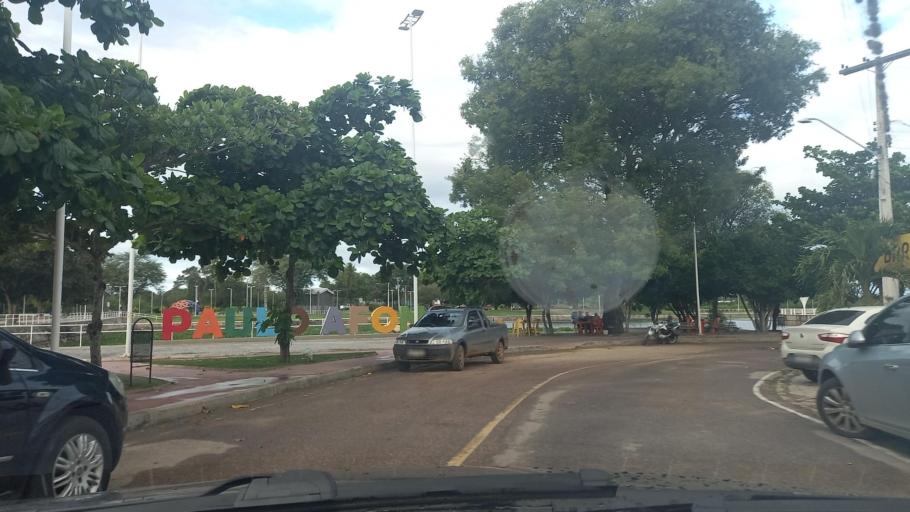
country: BR
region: Bahia
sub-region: Paulo Afonso
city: Paulo Afonso
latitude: -9.3971
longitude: -38.2138
